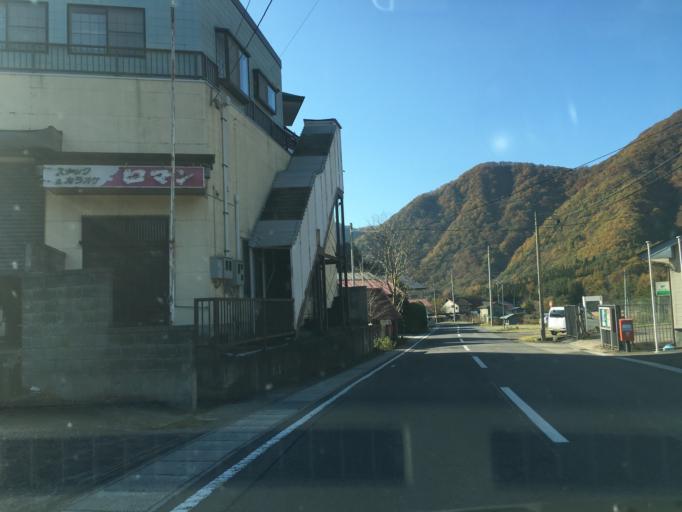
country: JP
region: Fukushima
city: Inawashiro
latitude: 37.2798
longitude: 139.9931
